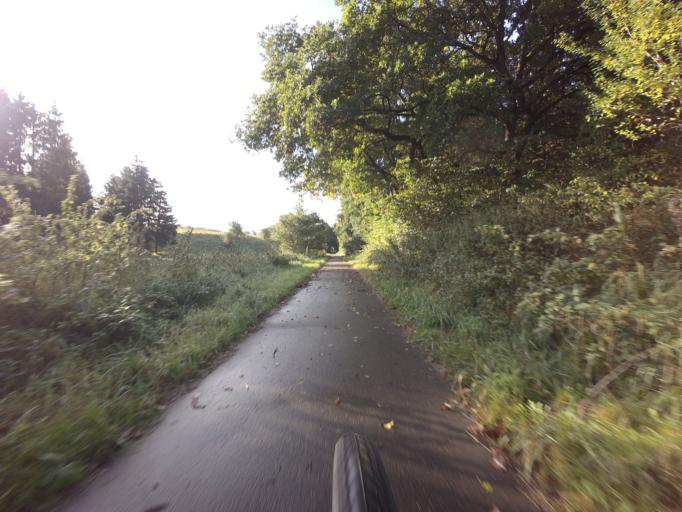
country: DK
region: Central Jutland
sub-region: Viborg Kommune
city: Bjerringbro
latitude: 56.4675
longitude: 9.5898
